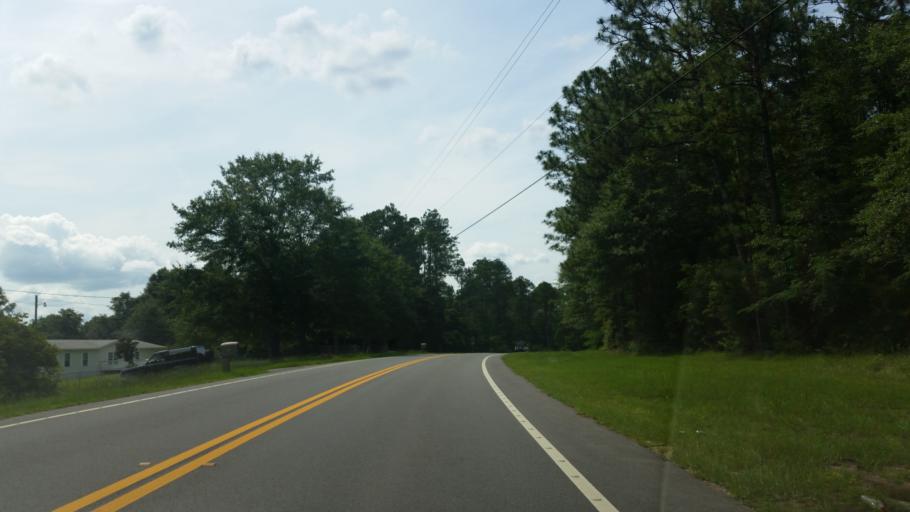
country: US
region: Florida
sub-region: Escambia County
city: Cantonment
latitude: 30.6345
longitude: -87.3817
